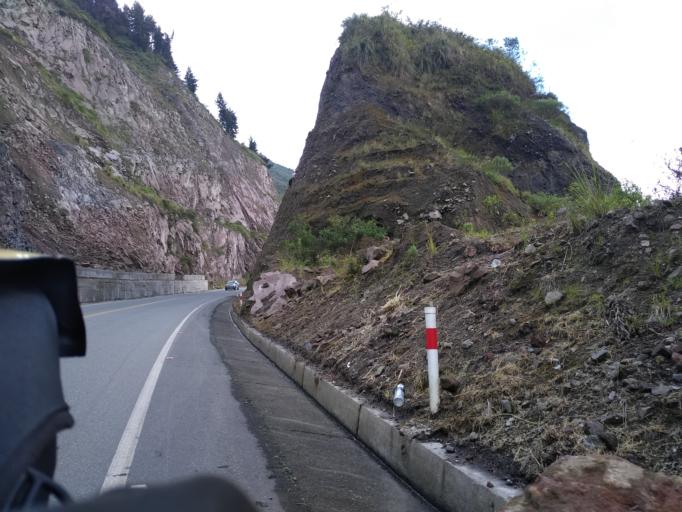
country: EC
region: Tungurahua
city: Banos
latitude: -1.4848
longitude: -78.5183
